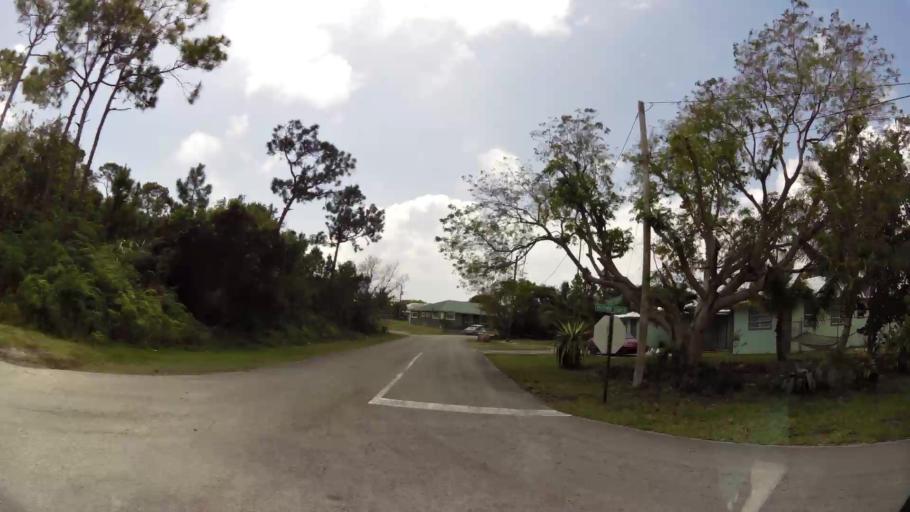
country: BS
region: Freeport
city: Lucaya
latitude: 26.5191
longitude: -78.6547
